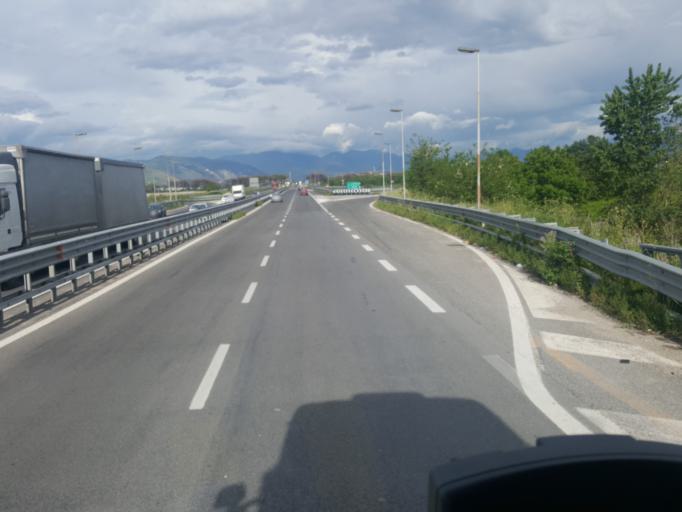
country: IT
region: Campania
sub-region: Provincia di Napoli
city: Pascarola
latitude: 40.9735
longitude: 14.3267
